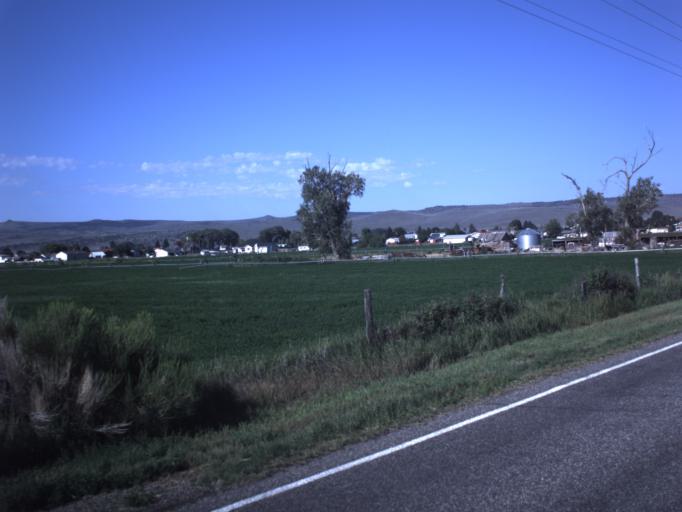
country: US
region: Utah
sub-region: Wayne County
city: Loa
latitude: 38.4117
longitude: -111.6333
